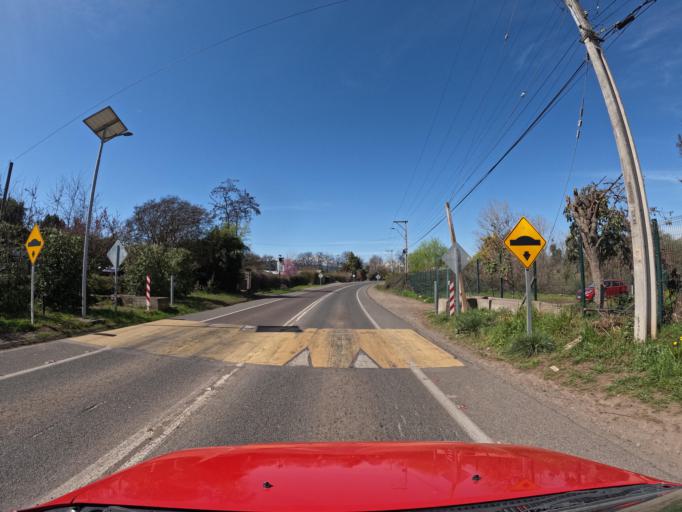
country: CL
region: Maule
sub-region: Provincia de Curico
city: Teno
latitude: -34.9689
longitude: -71.0122
